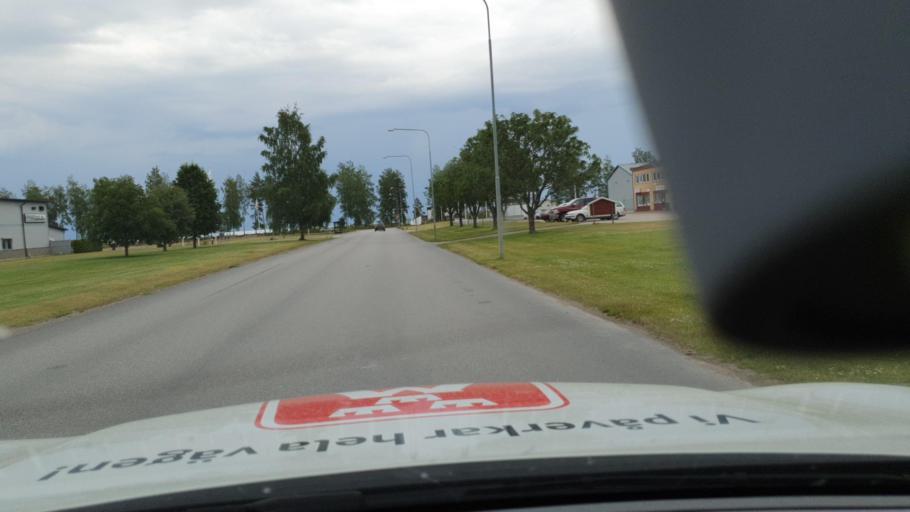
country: SE
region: Vaestra Goetaland
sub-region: Karlsborgs Kommun
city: Karlsborg
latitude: 58.5521
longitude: 14.4961
